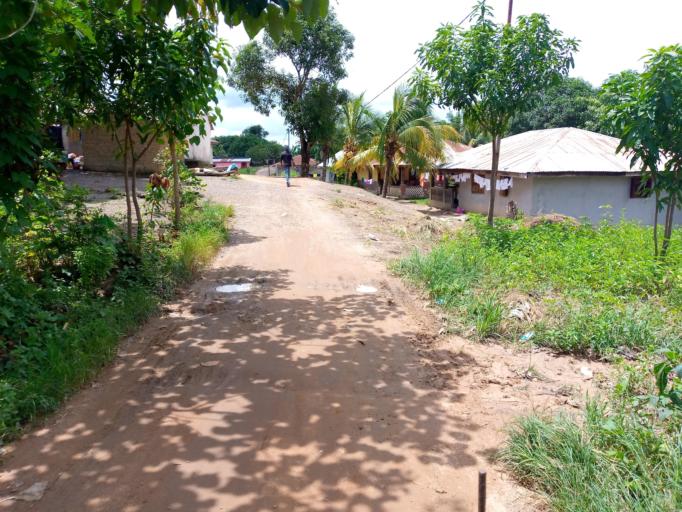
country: SL
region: Northern Province
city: Magburaka
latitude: 8.7281
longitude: -11.9408
